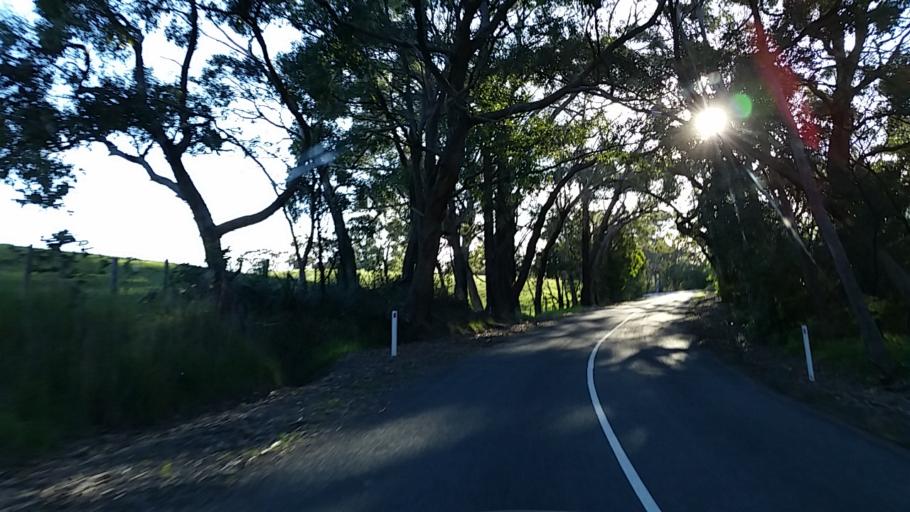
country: AU
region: South Australia
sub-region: Mount Barker
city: Meadows
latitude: -35.2251
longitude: 138.7327
